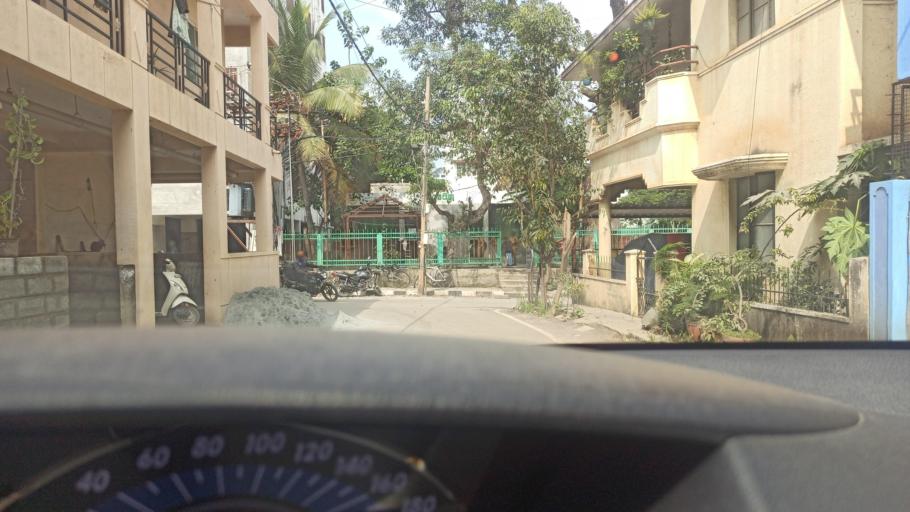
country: IN
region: Karnataka
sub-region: Bangalore Urban
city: Bangalore
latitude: 12.9883
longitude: 77.6849
